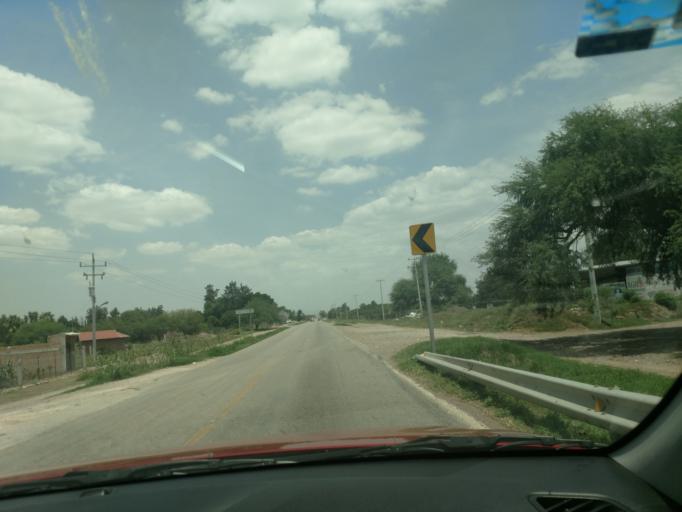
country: MX
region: San Luis Potosi
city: Ciudad Fernandez
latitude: 21.9502
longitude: -100.0627
